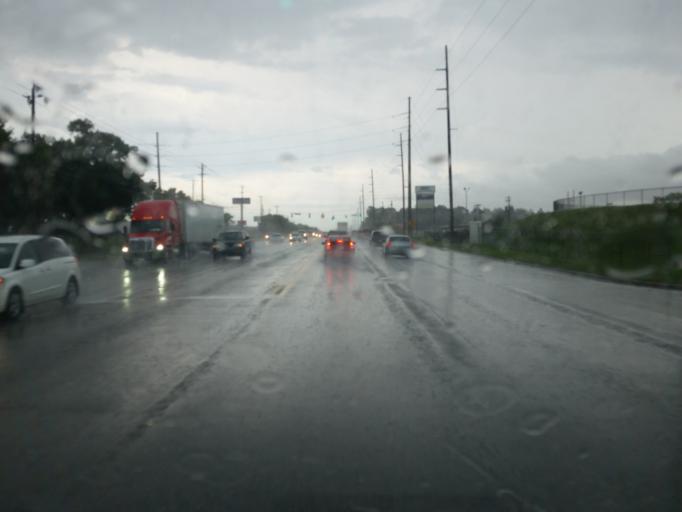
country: US
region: Alabama
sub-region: Mobile County
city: Prichard
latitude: 30.7201
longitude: -88.1531
